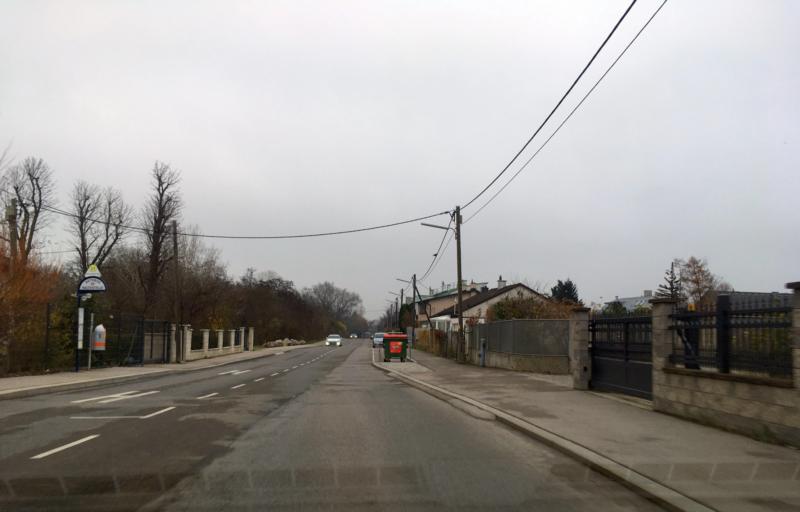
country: AT
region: Vienna
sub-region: Wien Stadt
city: Vienna
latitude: 48.2133
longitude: 16.4508
